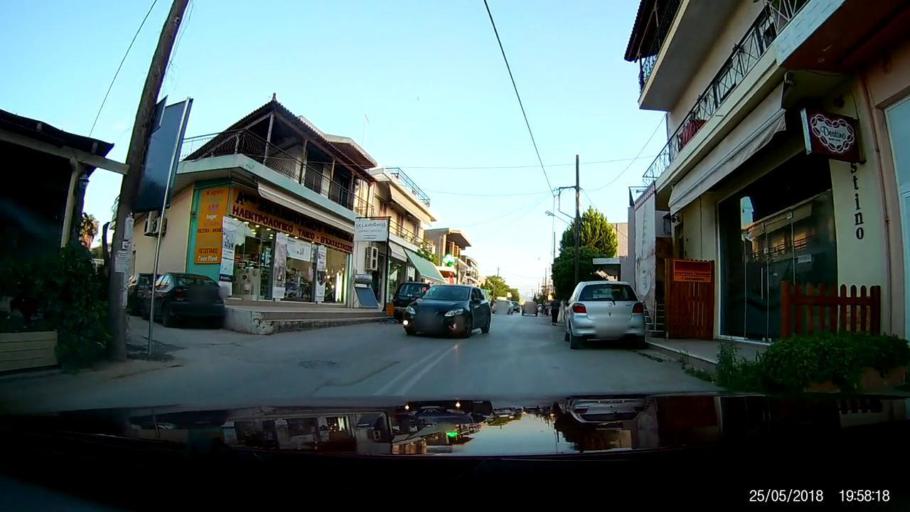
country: GR
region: Central Greece
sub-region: Nomos Evvoias
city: Vasilikon
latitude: 38.4255
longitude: 23.6708
